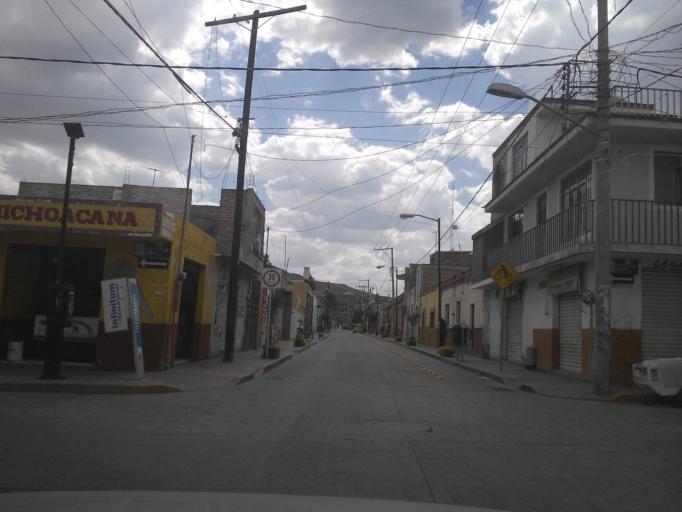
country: MX
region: Guanajuato
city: San Francisco del Rincon
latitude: 21.0301
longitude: -101.8803
